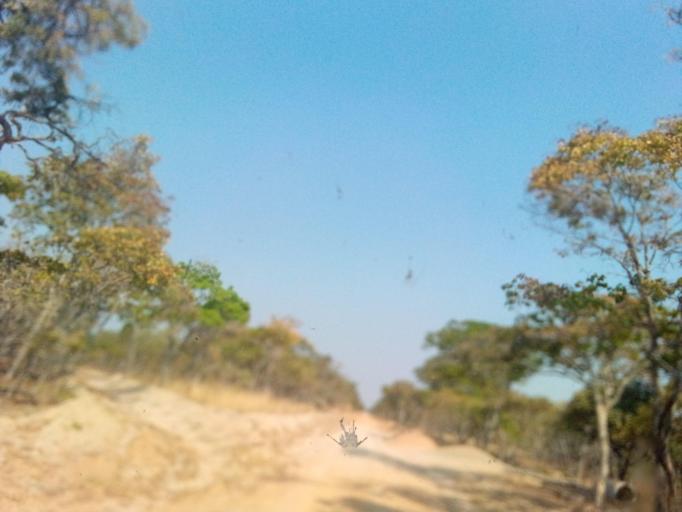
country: ZM
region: Northern
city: Mpika
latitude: -12.2305
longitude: 30.9220
